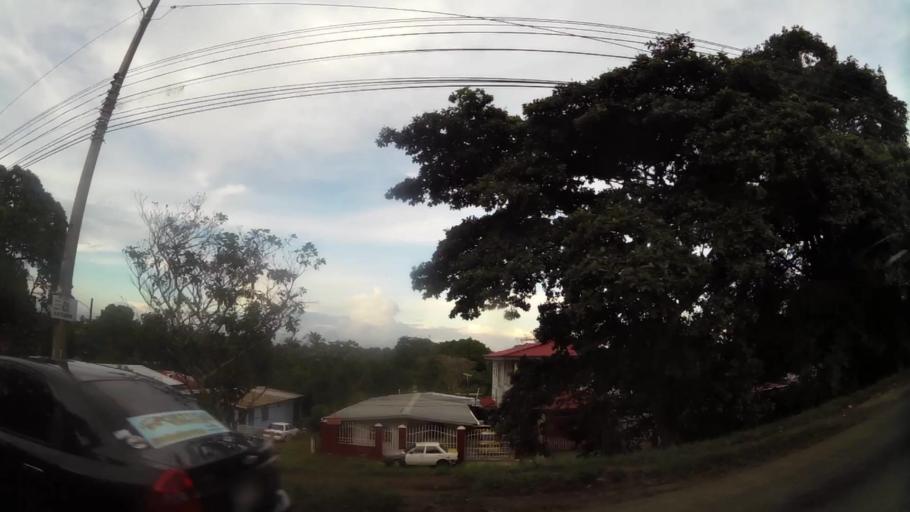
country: PA
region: Panama
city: La Chorrera
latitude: 8.8694
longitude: -79.7710
